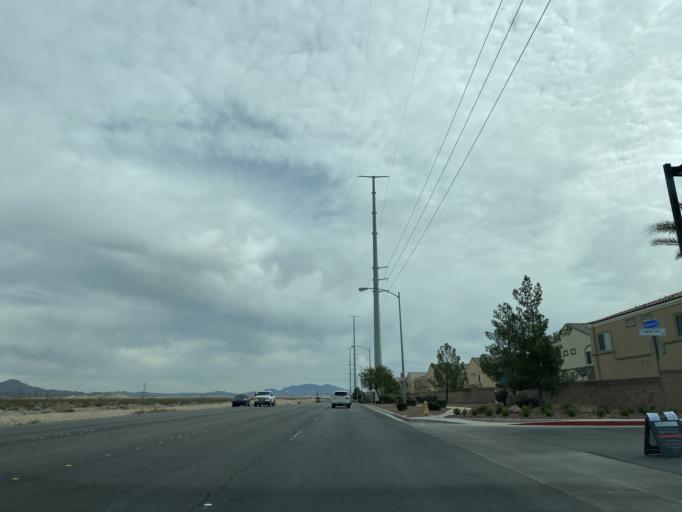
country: US
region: Nevada
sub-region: Clark County
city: Nellis Air Force Base
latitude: 36.2766
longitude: -115.0872
